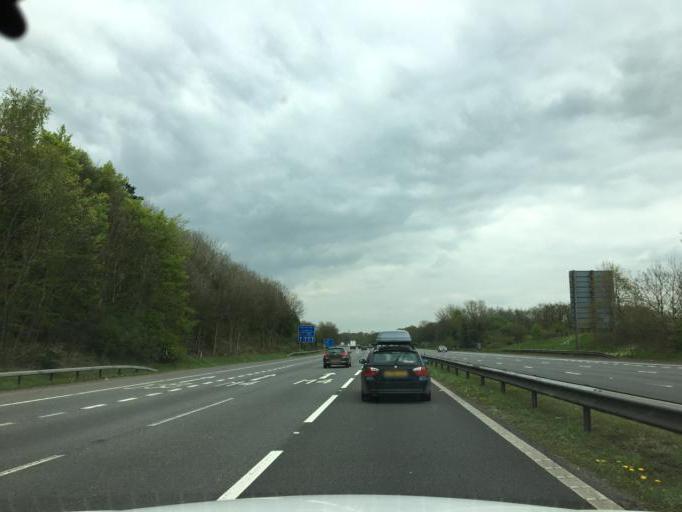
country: GB
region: Wales
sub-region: Rhondda Cynon Taf
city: Llantrisant
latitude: 51.5091
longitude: -3.3506
